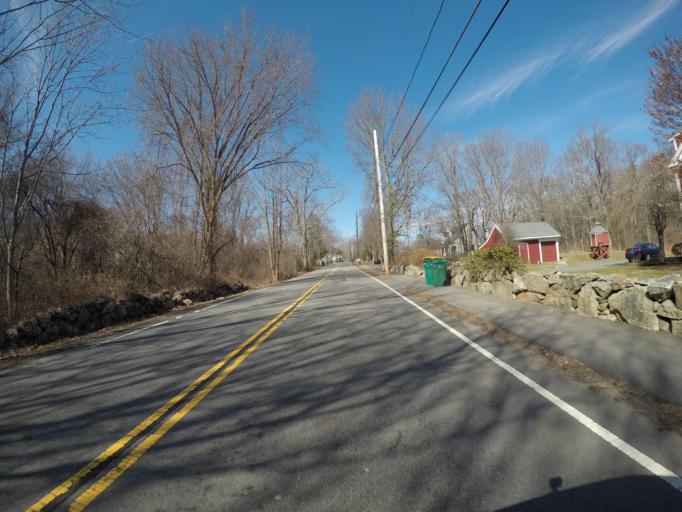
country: US
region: Massachusetts
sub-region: Norfolk County
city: Stoughton
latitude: 42.0742
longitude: -71.1116
